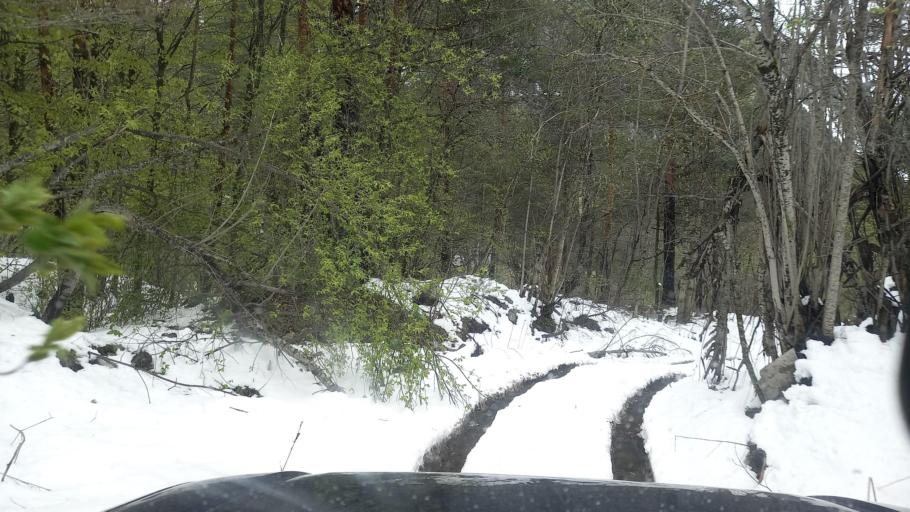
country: RU
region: North Ossetia
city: Mizur
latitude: 42.7903
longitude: 43.9129
